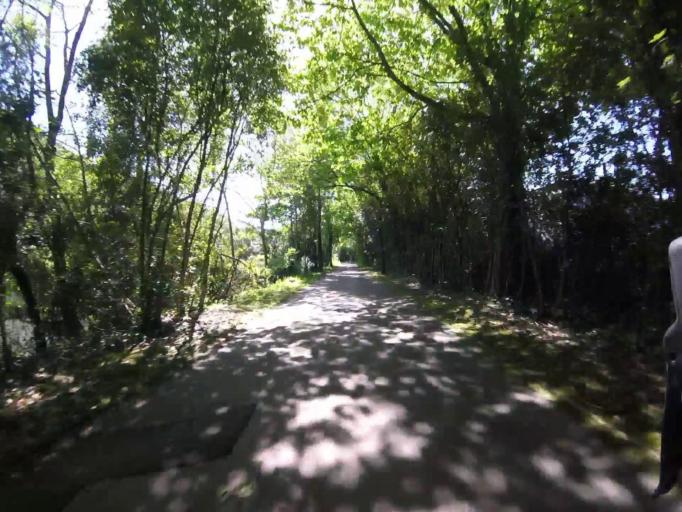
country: ES
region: Basque Country
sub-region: Provincia de Guipuzcoa
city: Irun
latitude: 43.3428
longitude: -1.7562
